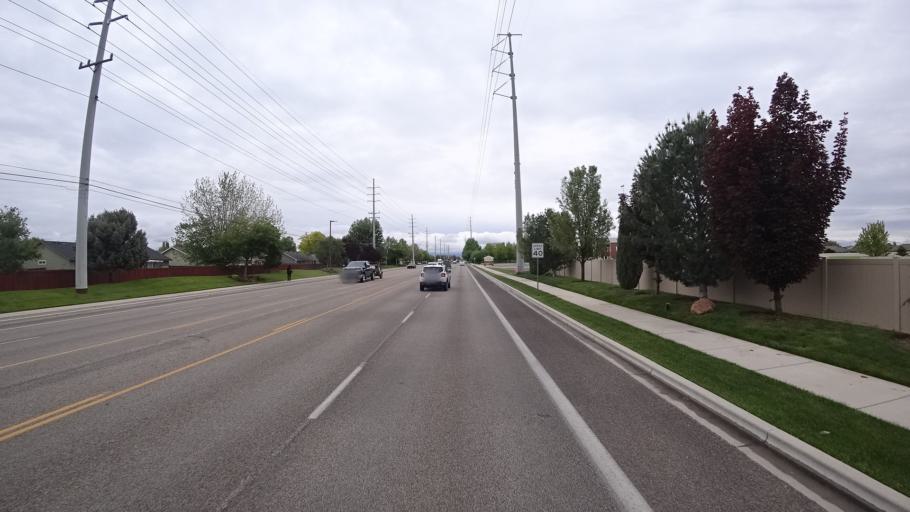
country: US
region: Idaho
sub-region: Ada County
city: Meridian
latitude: 43.6483
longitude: -116.3626
